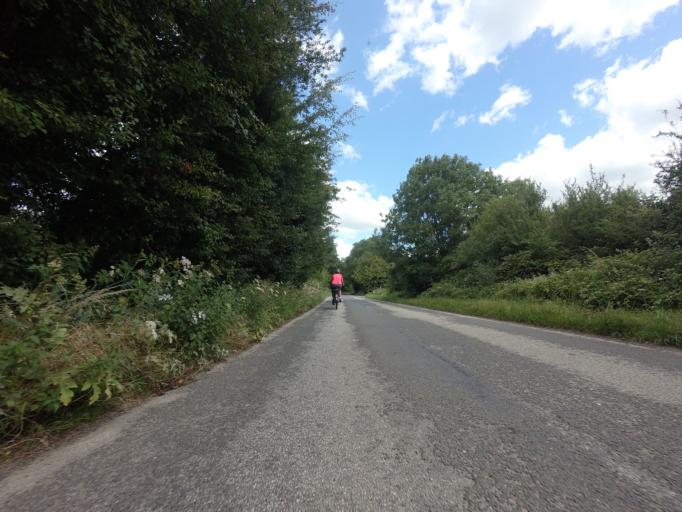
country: GB
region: England
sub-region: East Sussex
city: Hailsham
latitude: 50.8400
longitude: 0.1789
